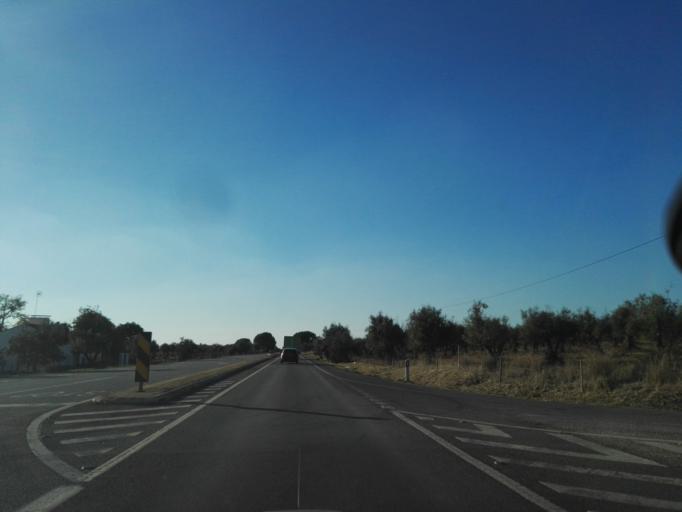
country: PT
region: Evora
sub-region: Estremoz
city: Estremoz
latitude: 38.8263
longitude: -7.5227
